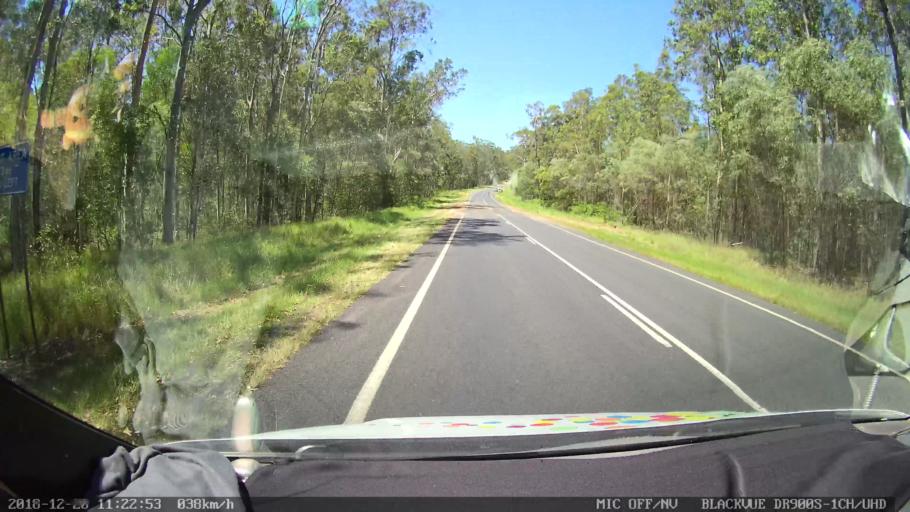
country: AU
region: New South Wales
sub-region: Richmond Valley
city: Casino
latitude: -29.0625
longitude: 153.0048
